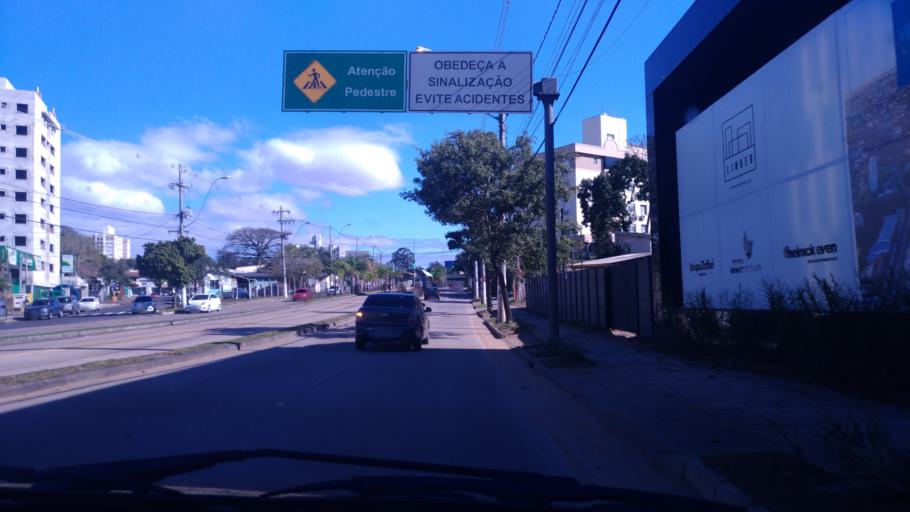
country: BR
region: Rio Grande do Sul
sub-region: Porto Alegre
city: Porto Alegre
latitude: -30.0756
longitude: -51.2055
